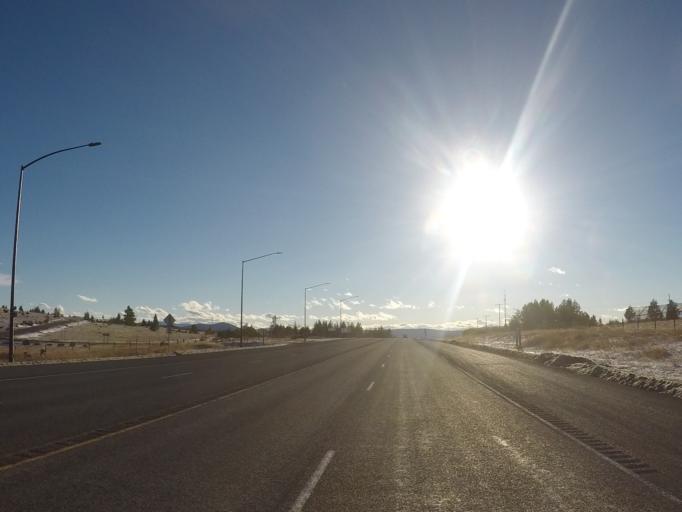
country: US
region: Montana
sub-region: Lewis and Clark County
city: Helena West Side
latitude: 46.5623
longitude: -112.3076
